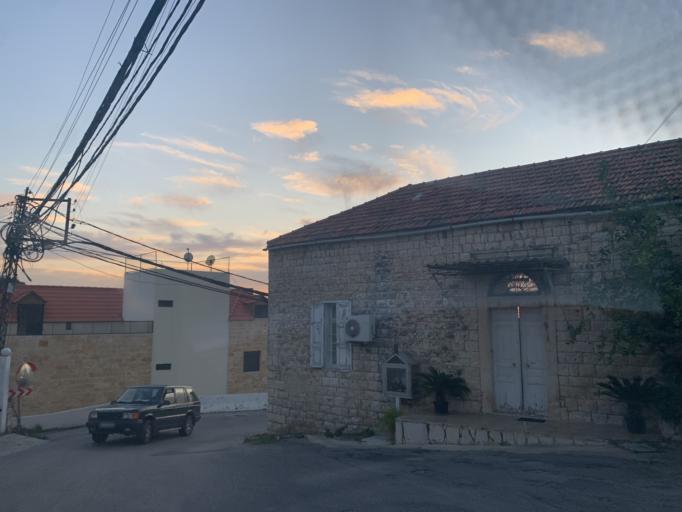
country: LB
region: Mont-Liban
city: Djounie
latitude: 34.0437
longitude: 35.6364
